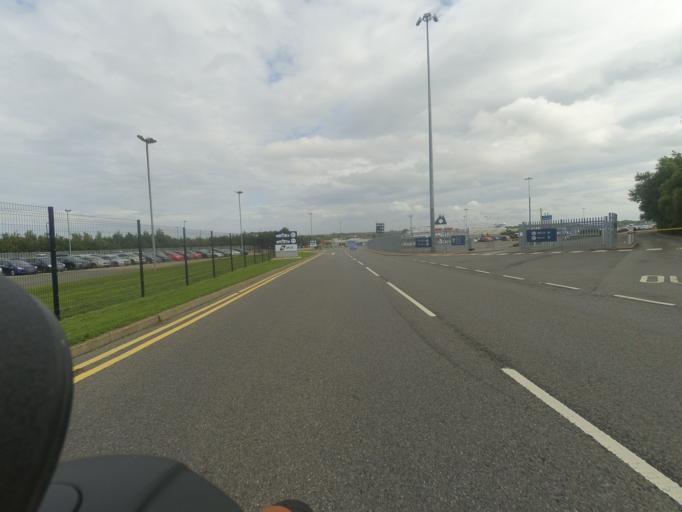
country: GB
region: England
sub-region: Borough of North Tyneside
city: North Shields
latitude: 54.9937
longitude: -1.4563
